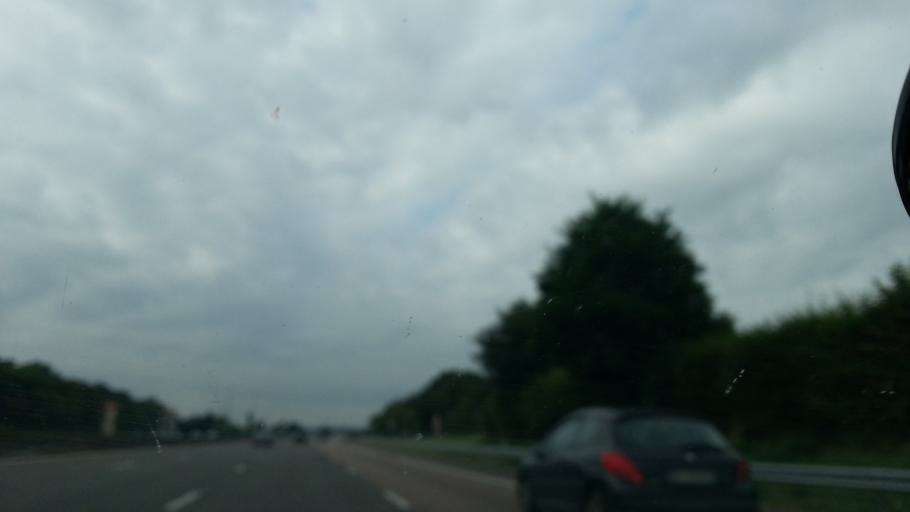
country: FR
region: Bourgogne
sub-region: Departement de la Cote-d'Or
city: Bligny-les-Beaune
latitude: 46.9613
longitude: 4.8363
